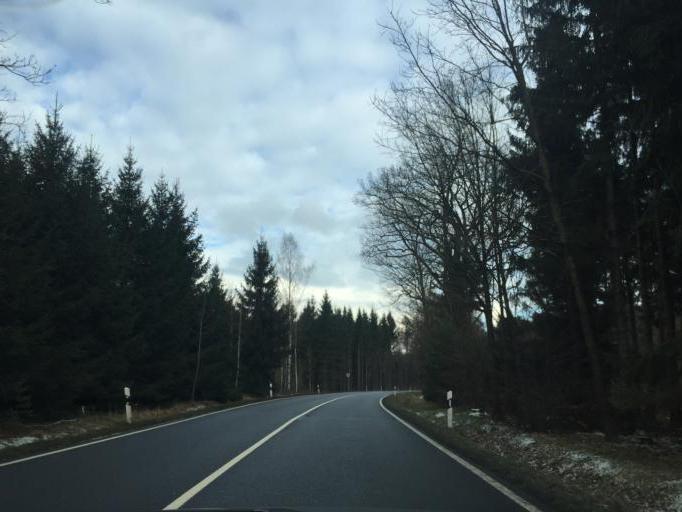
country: DE
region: Saxony
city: Radeberg
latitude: 51.1055
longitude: 13.8733
